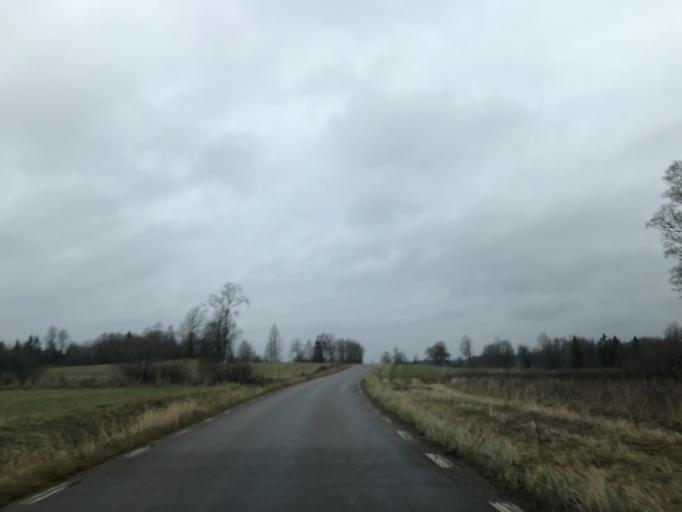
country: SE
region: Vaestra Goetaland
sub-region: Ulricehamns Kommun
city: Ulricehamn
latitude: 57.8870
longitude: 13.5118
